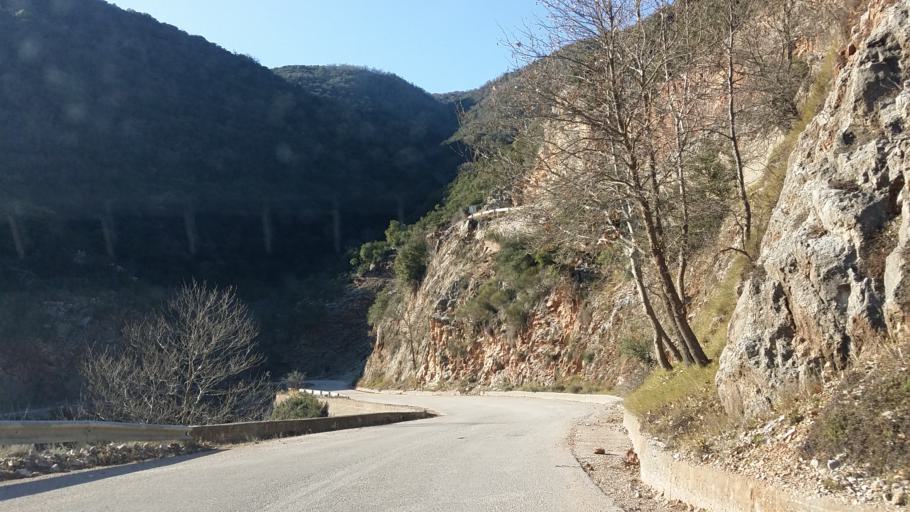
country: GR
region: Central Greece
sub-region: Nomos Evrytanias
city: Kerasochori
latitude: 38.9141
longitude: 21.6034
